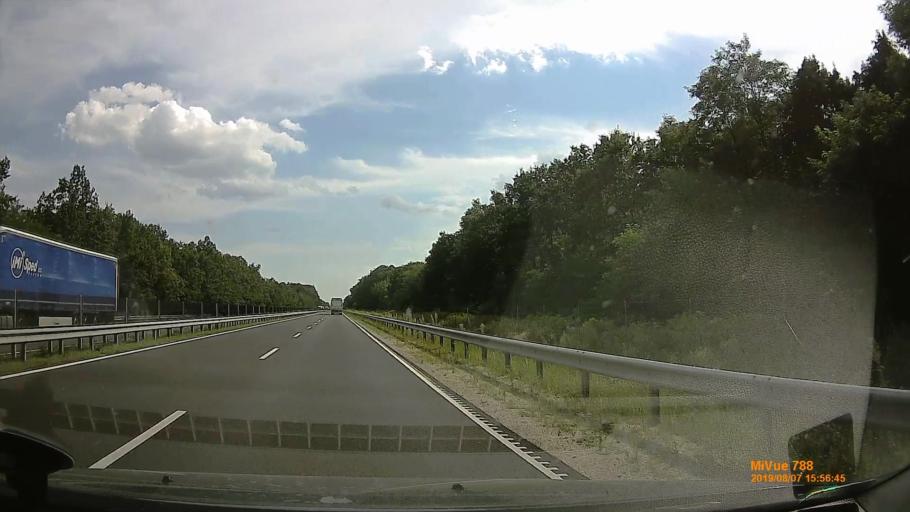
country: HU
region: Vas
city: Kormend
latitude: 47.0552
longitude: 16.6152
